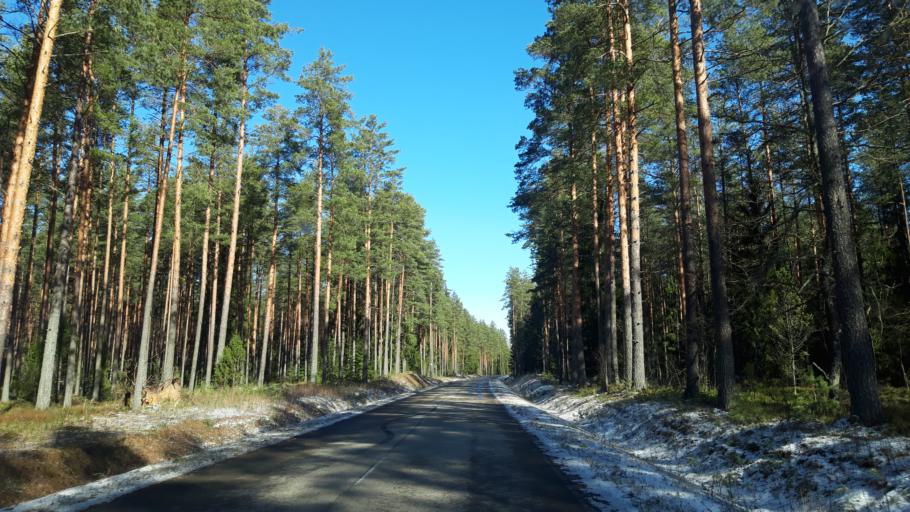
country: LV
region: Strenci
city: Strenci
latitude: 57.5807
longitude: 25.7135
